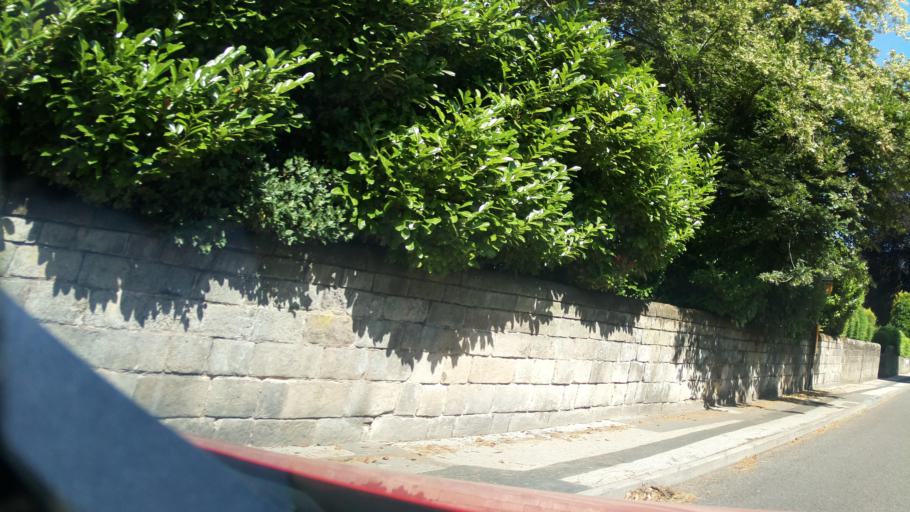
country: GB
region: England
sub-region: Derby
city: Derby
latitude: 52.9334
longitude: -1.4841
